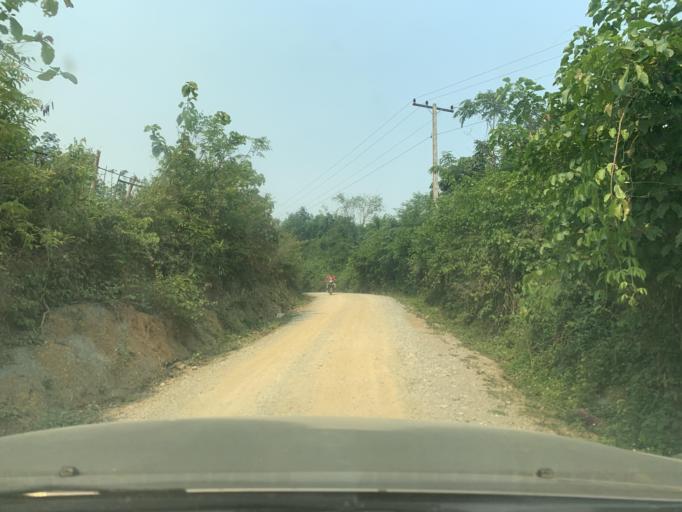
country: LA
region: Louangphabang
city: Louangphabang
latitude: 19.8907
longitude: 102.2506
